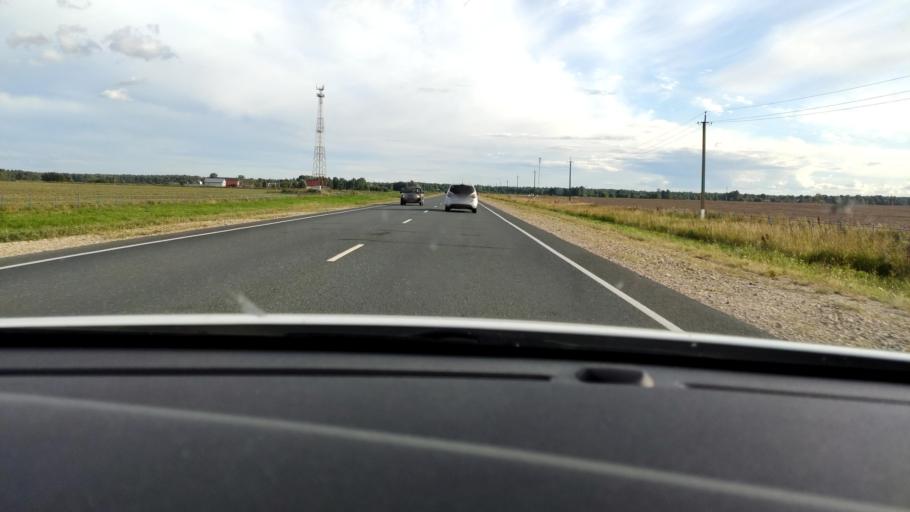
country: RU
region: Mariy-El
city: Krasnogorskiy
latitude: 56.2058
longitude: 48.2358
